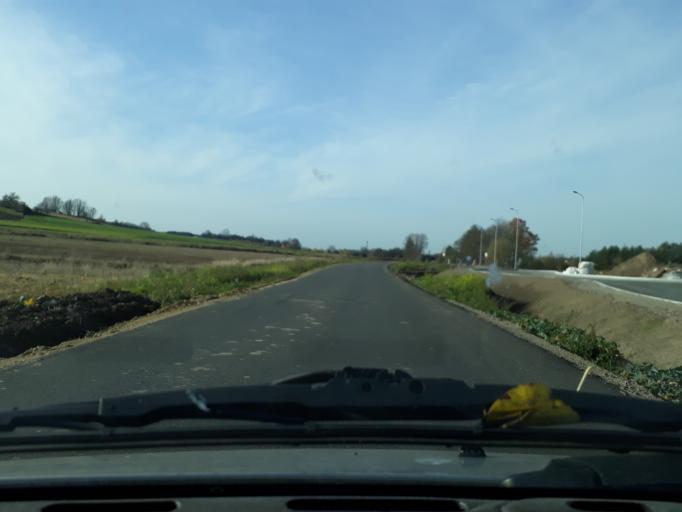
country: PL
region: Silesian Voivodeship
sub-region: Powiat myszkowski
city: Gniazdow
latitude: 50.5904
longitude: 19.0872
